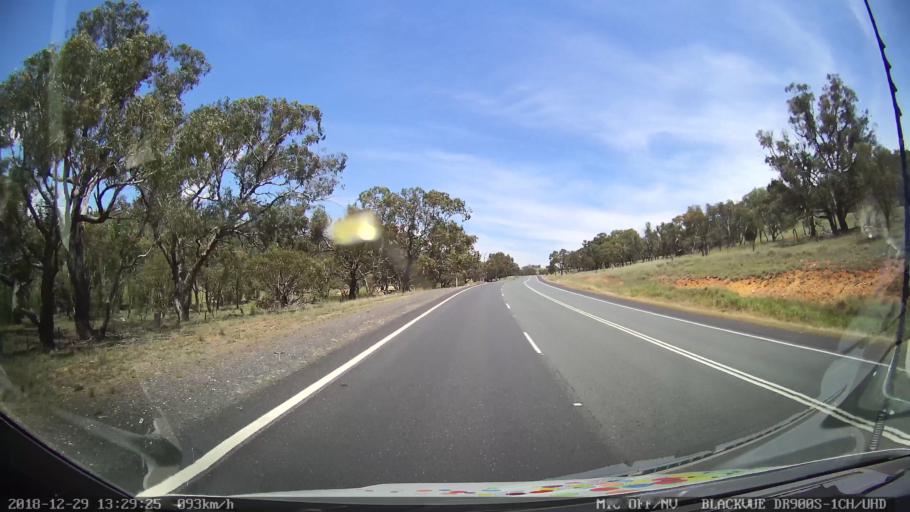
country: AU
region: New South Wales
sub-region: Cooma-Monaro
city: Cooma
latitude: -35.8898
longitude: 149.1617
